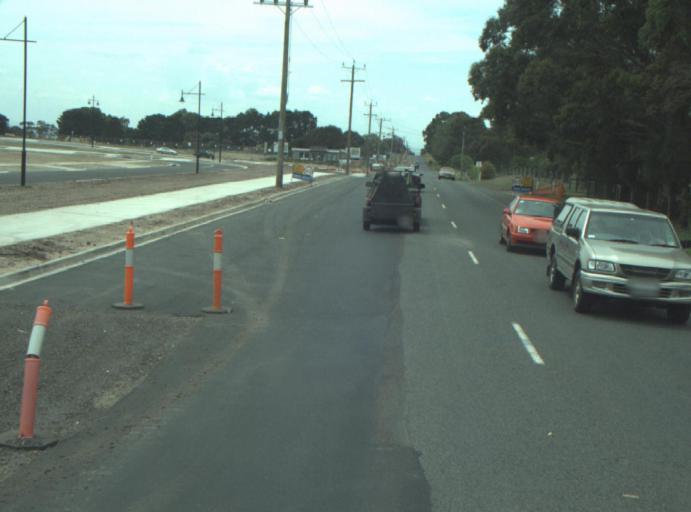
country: AU
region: Victoria
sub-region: Greater Geelong
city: Clifton Springs
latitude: -38.1739
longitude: 144.5522
